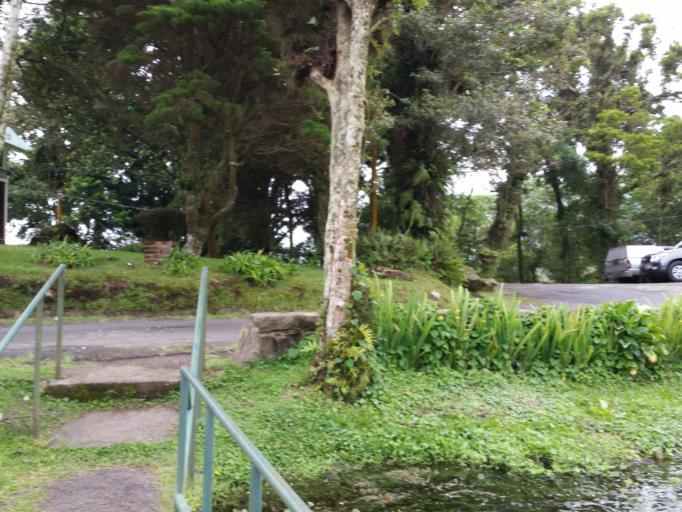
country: NI
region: Matagalpa
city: Matagalpa
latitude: 12.9987
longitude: -85.9105
